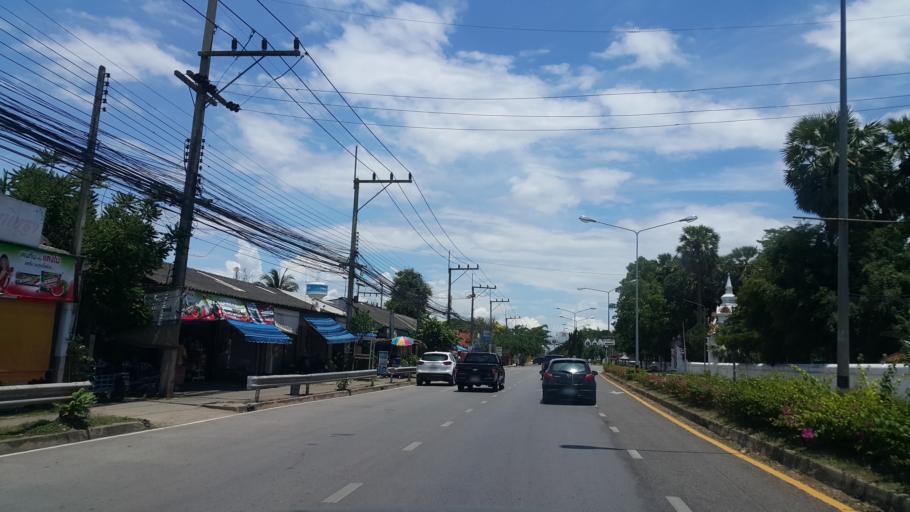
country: TH
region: Phayao
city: Phayao
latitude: 19.1775
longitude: 99.8896
